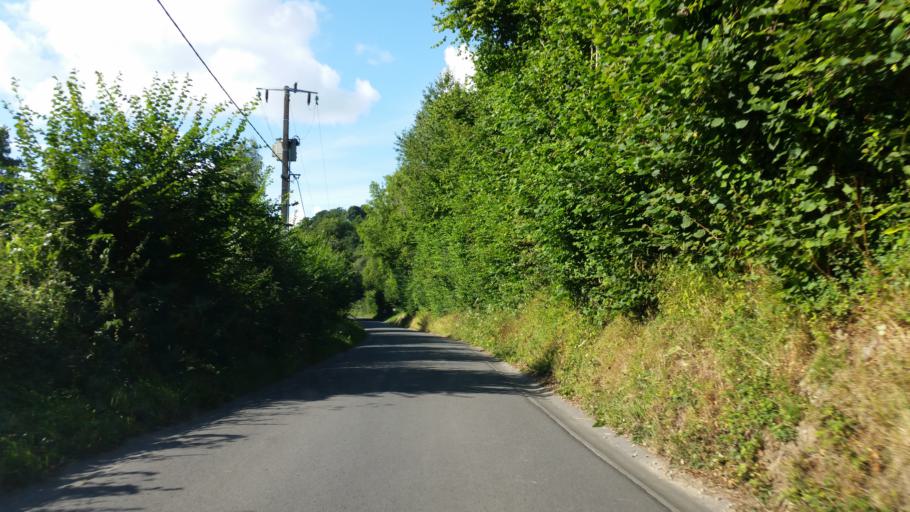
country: FR
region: Lower Normandy
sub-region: Departement du Calvados
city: Equemauville
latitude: 49.3914
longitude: 0.2271
